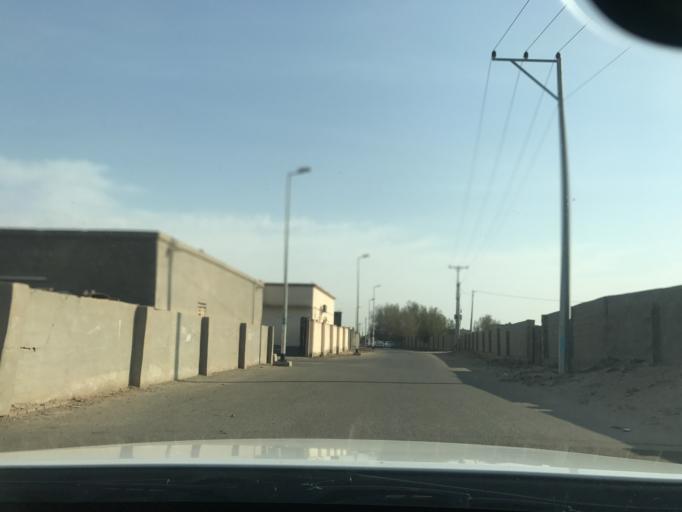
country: SA
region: Makkah
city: Al Jumum
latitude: 21.4516
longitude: 39.5350
